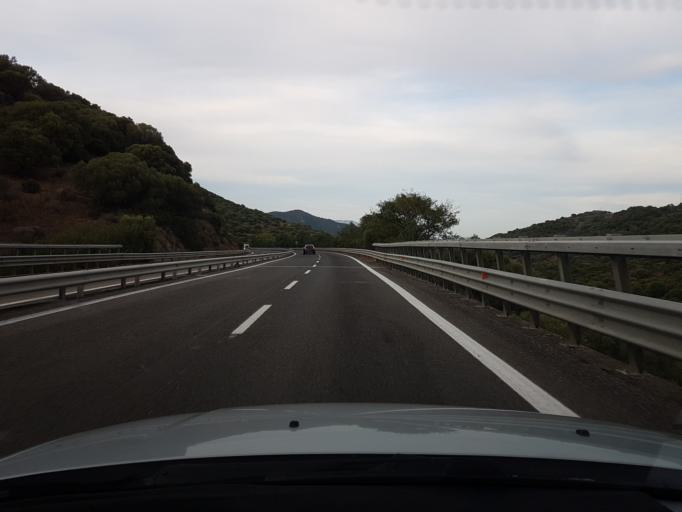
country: IT
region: Sardinia
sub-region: Provincia di Nuoro
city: Nuoro
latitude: 40.3534
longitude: 9.3431
